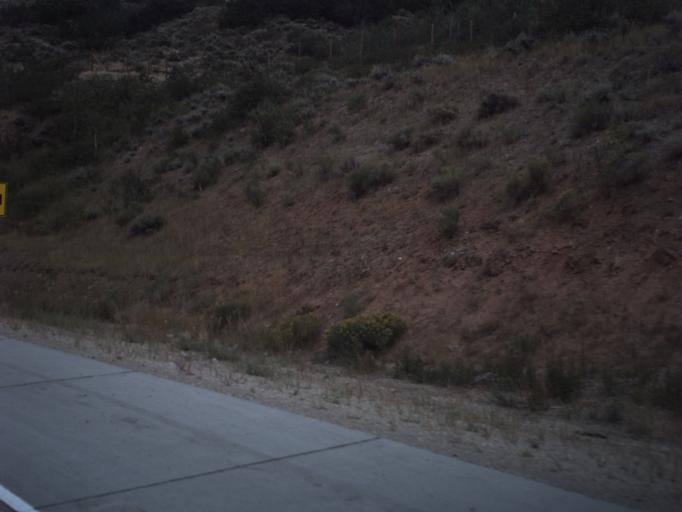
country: US
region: Utah
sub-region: Summit County
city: Snyderville
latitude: 40.7664
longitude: -111.4687
